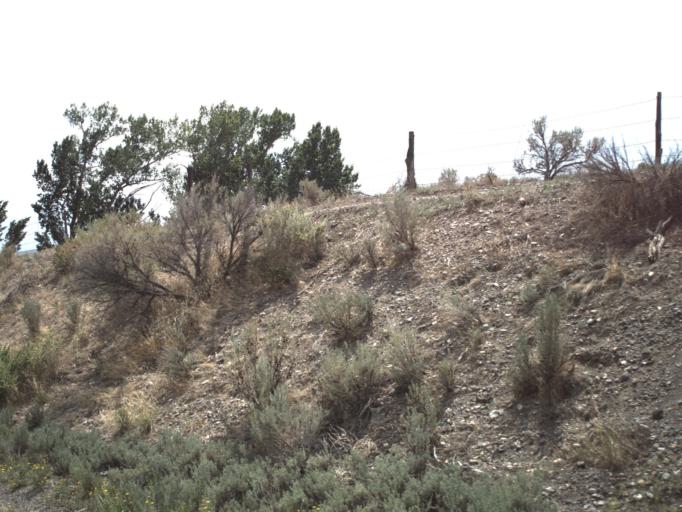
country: US
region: Utah
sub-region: Piute County
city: Junction
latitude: 38.1593
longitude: -112.0068
